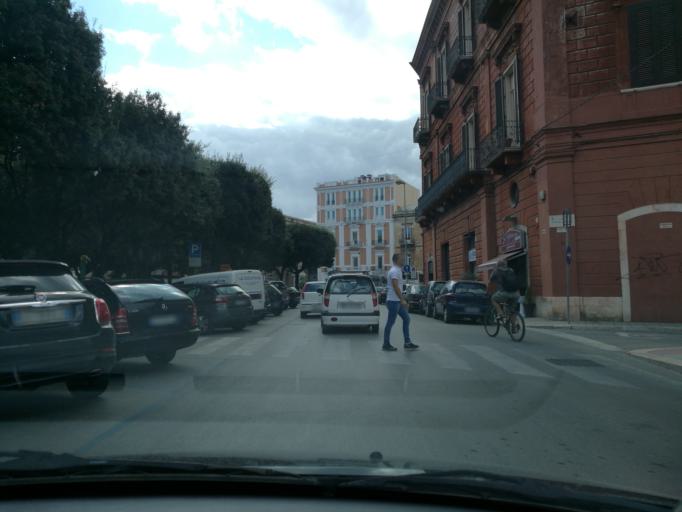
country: IT
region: Apulia
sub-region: Provincia di Bari
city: Bari
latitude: 41.1267
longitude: 16.8660
